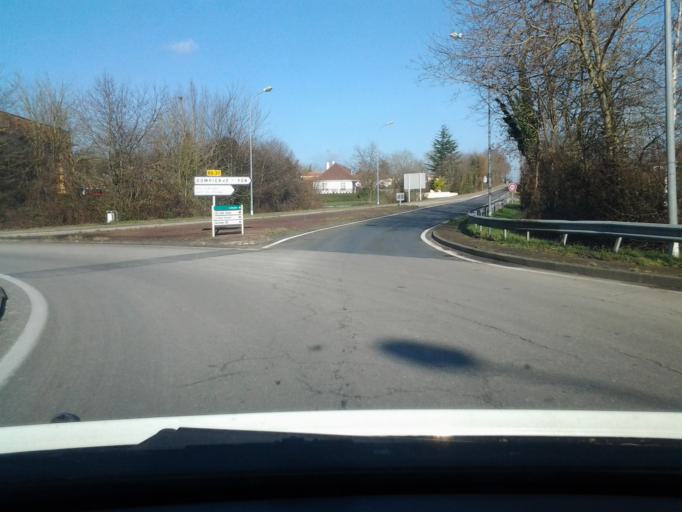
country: FR
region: Pays de la Loire
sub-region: Departement de la Vendee
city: La Roche-sur-Yon
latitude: 46.6967
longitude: -1.4239
